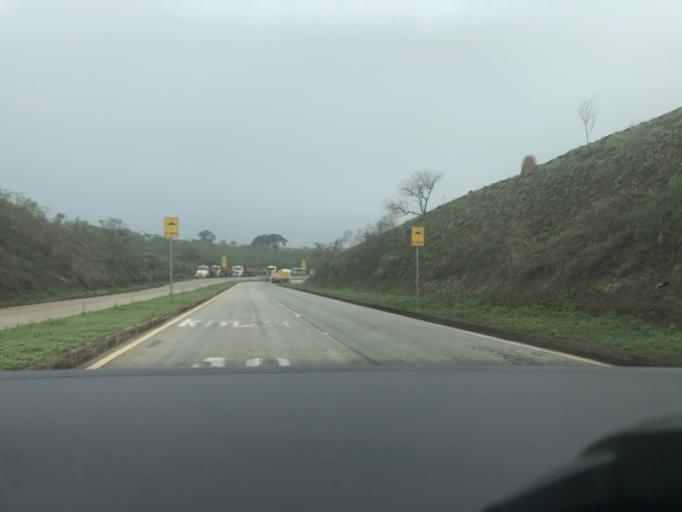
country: BR
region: Minas Gerais
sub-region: Congonhas
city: Congonhas
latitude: -20.5945
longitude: -43.9564
